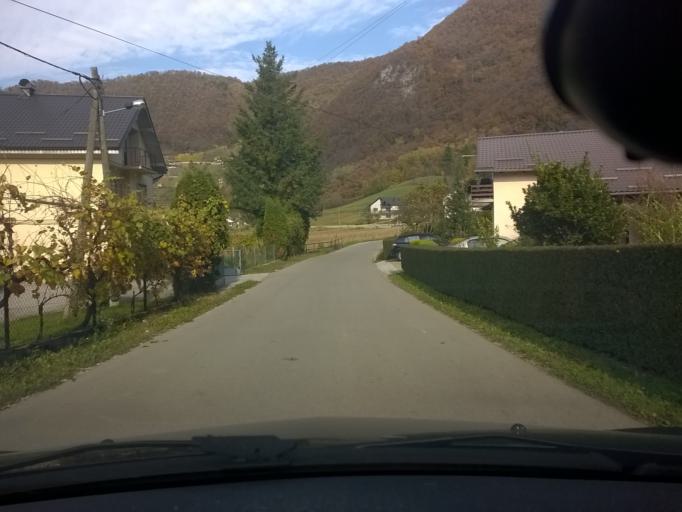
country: HR
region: Krapinsko-Zagorska
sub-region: Grad Krapina
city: Krapina
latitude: 46.1767
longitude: 15.8691
